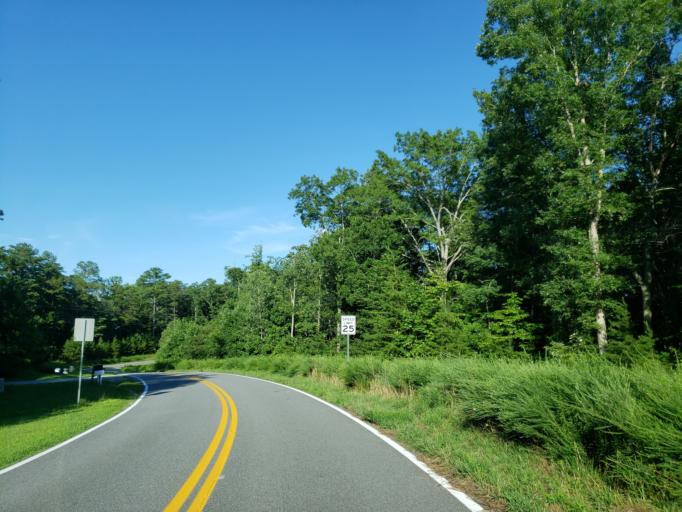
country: US
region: Georgia
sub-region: Bartow County
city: Rydal
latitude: 34.3539
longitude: -84.6048
